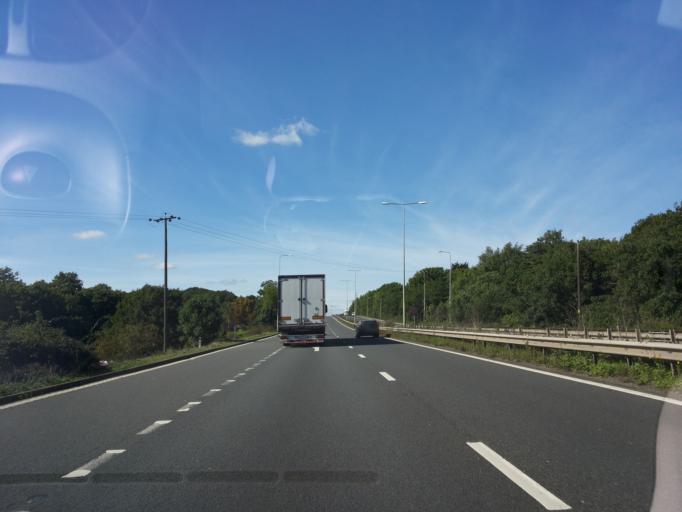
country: GB
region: England
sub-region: Kent
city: Dunkirk
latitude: 51.2889
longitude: 1.0015
